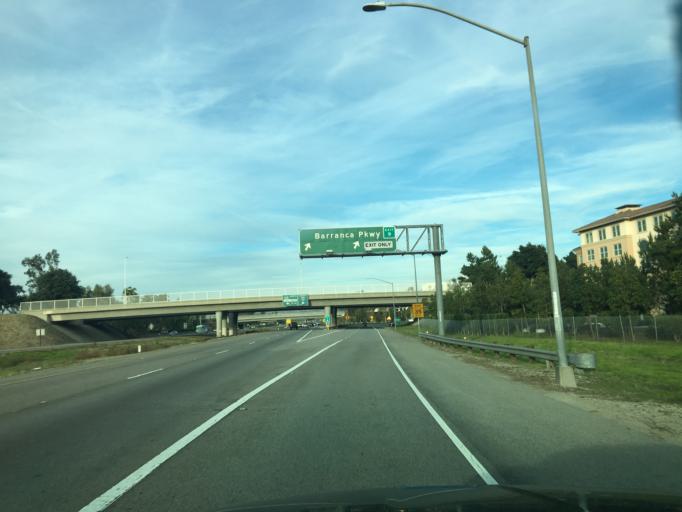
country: US
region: California
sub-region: Orange County
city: Laguna Woods
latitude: 33.6554
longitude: -117.7589
